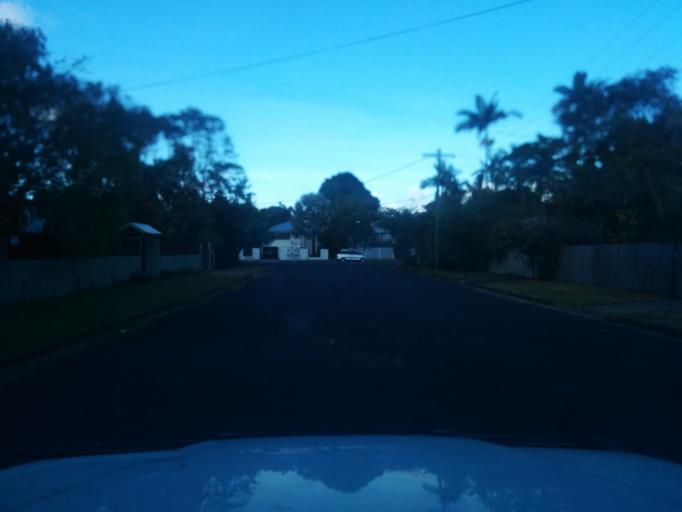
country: AU
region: Queensland
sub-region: Cairns
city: Woree
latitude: -16.9415
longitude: 145.7388
